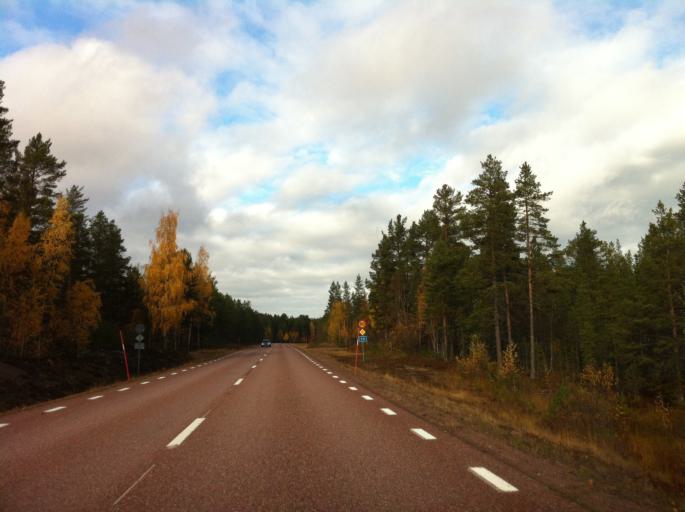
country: SE
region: Dalarna
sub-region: Alvdalens Kommun
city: AElvdalen
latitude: 61.5246
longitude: 13.3626
